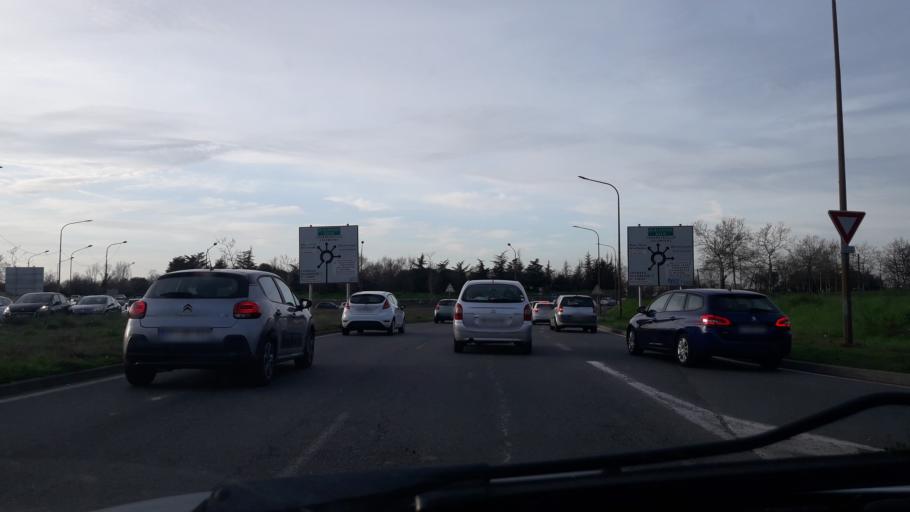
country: FR
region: Midi-Pyrenees
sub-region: Departement de la Haute-Garonne
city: Cugnaux
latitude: 43.5681
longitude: 1.3765
